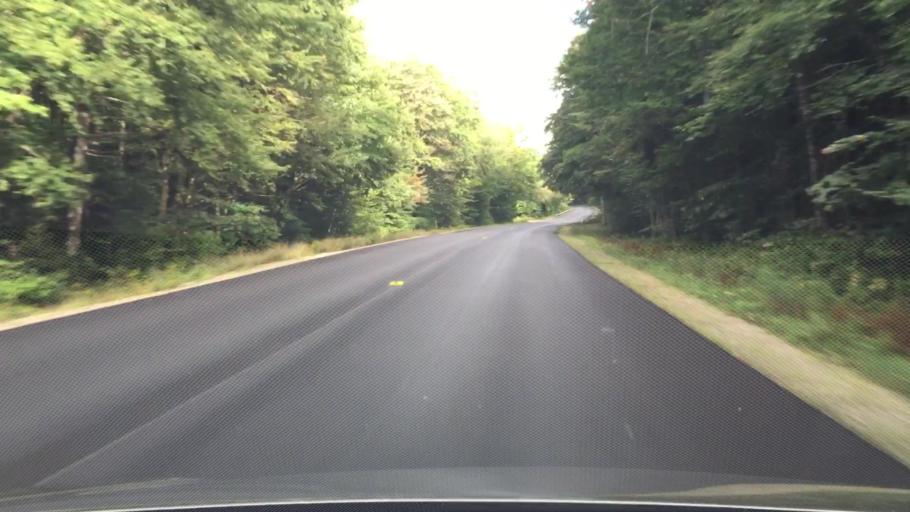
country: US
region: New Hampshire
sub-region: Carroll County
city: Tamworth
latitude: 43.9997
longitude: -71.4018
